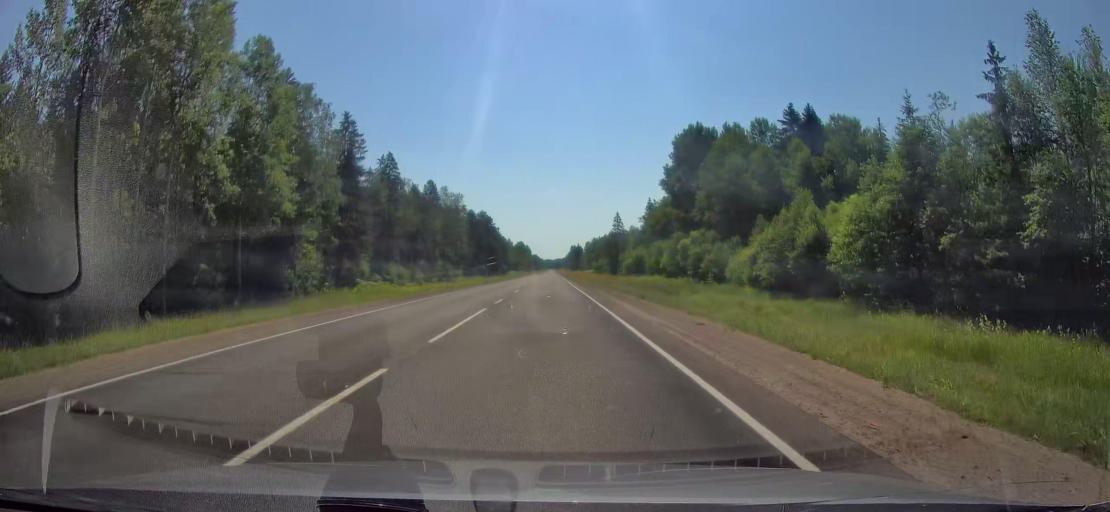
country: RU
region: Vologda
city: Chagoda
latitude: 59.0321
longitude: 35.3709
